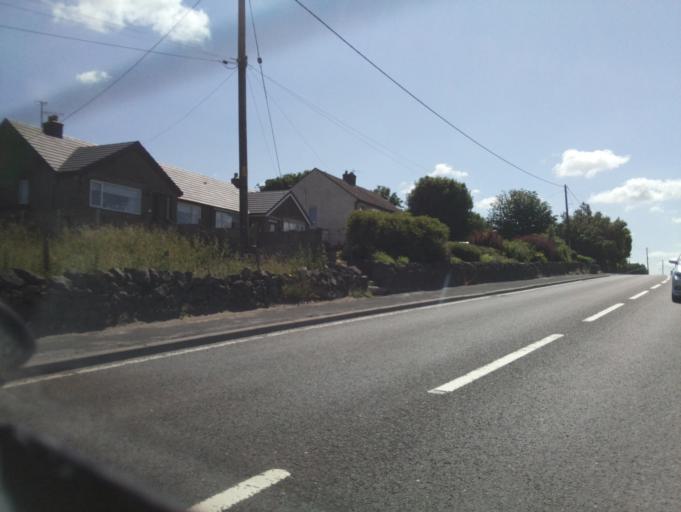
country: GB
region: England
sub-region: Derbyshire
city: Chapel en le Frith
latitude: 53.2961
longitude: -1.8885
